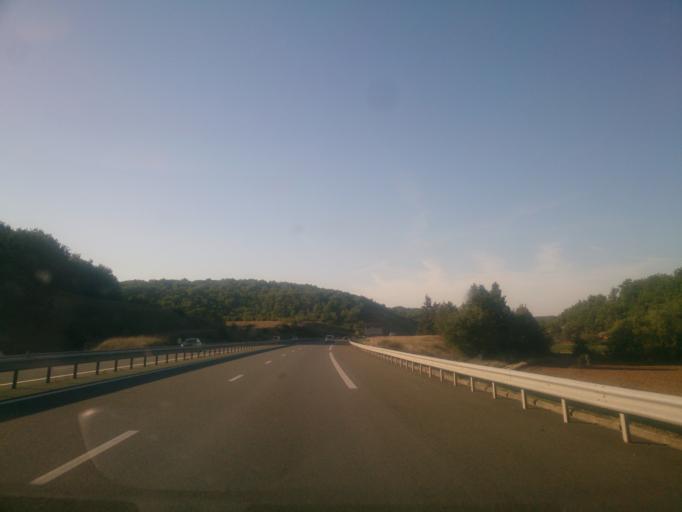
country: FR
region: Midi-Pyrenees
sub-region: Departement du Lot
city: Le Vigan
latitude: 44.7516
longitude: 1.5418
